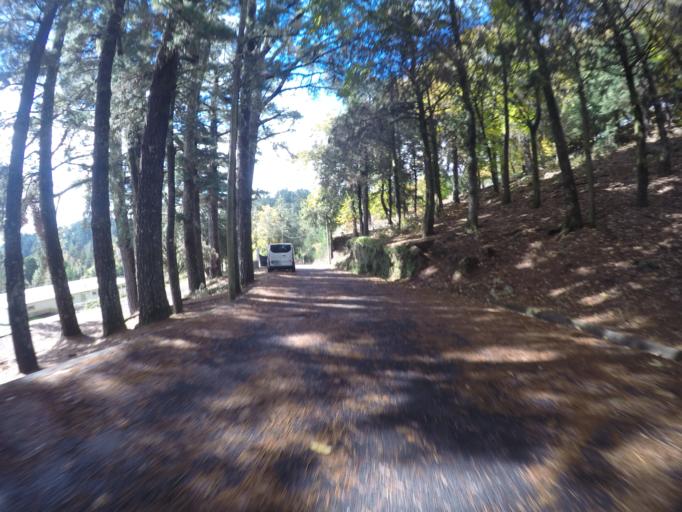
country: PT
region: Madeira
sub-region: Funchal
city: Nossa Senhora do Monte
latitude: 32.7047
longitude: -16.8890
